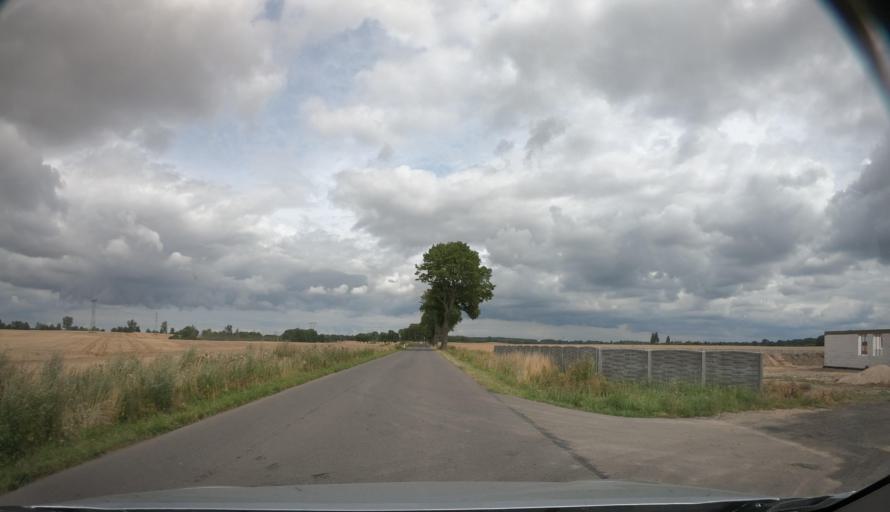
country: PL
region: West Pomeranian Voivodeship
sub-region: Koszalin
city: Koszalin
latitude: 54.1460
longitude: 16.0837
